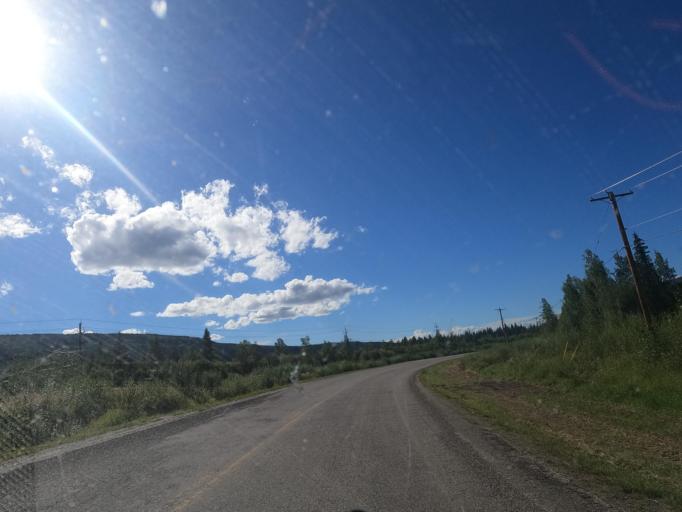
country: CA
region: Yukon
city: Dawson City
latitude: 64.0301
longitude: -139.1813
